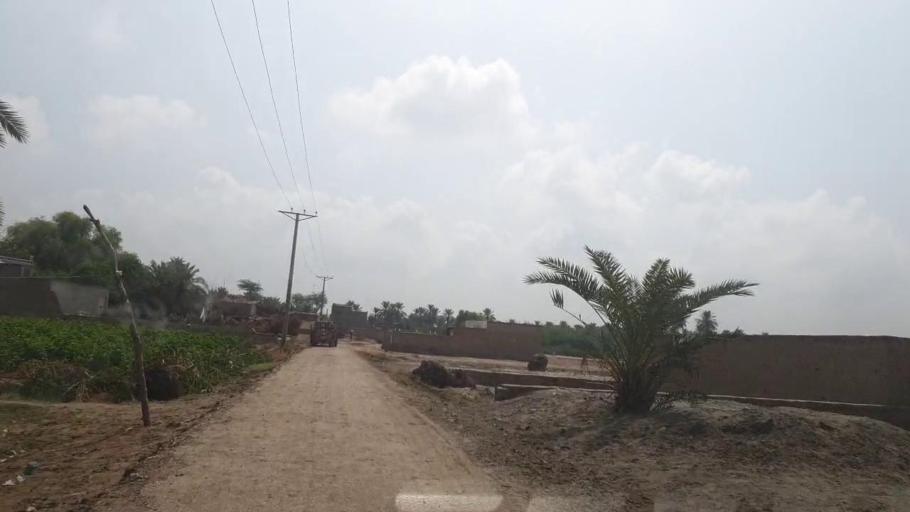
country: PK
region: Sindh
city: Khairpur
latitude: 27.5107
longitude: 68.7474
